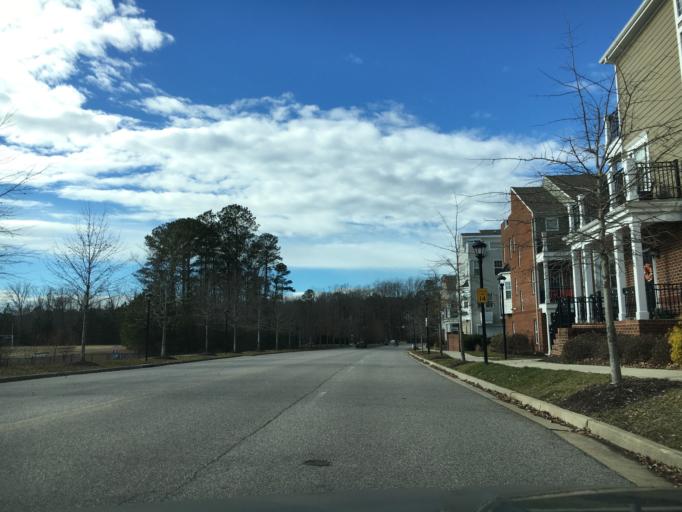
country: US
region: Virginia
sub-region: Henrico County
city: Short Pump
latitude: 37.6473
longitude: -77.6065
